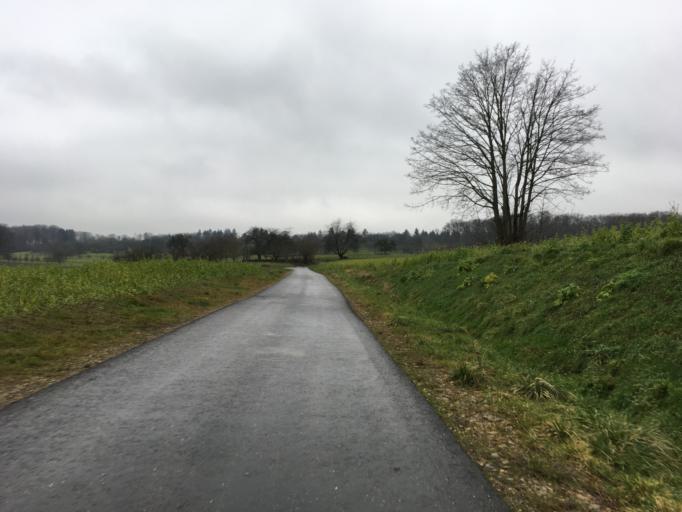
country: DE
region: Baden-Wuerttemberg
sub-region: Karlsruhe Region
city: Konigsbach-Stein
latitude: 48.9467
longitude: 8.5289
